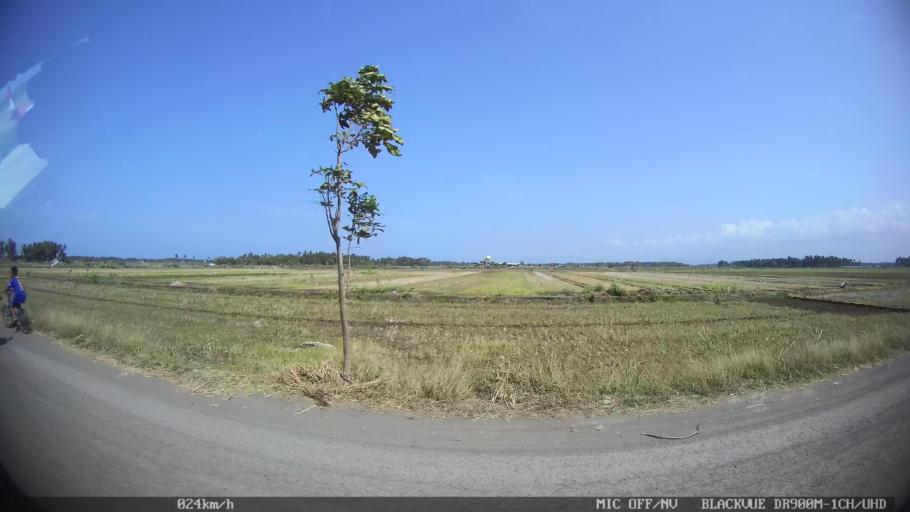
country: ID
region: Daerah Istimewa Yogyakarta
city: Srandakan
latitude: -7.9704
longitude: 110.2110
